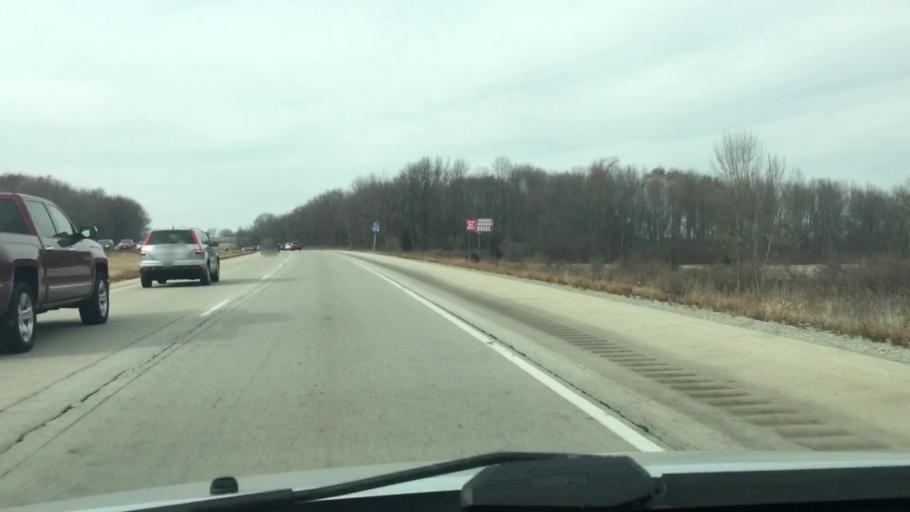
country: US
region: Wisconsin
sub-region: Jefferson County
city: Ixonia
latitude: 43.0803
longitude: -88.5984
